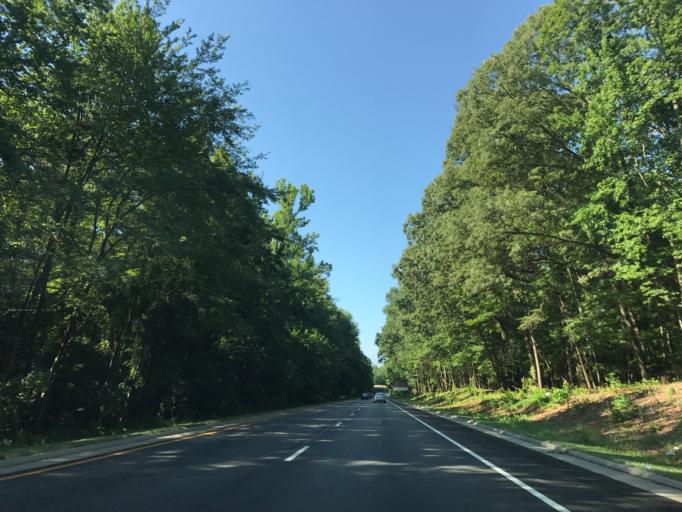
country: US
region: Maryland
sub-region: Prince George's County
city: Greenbelt
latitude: 39.0108
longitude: -76.8618
